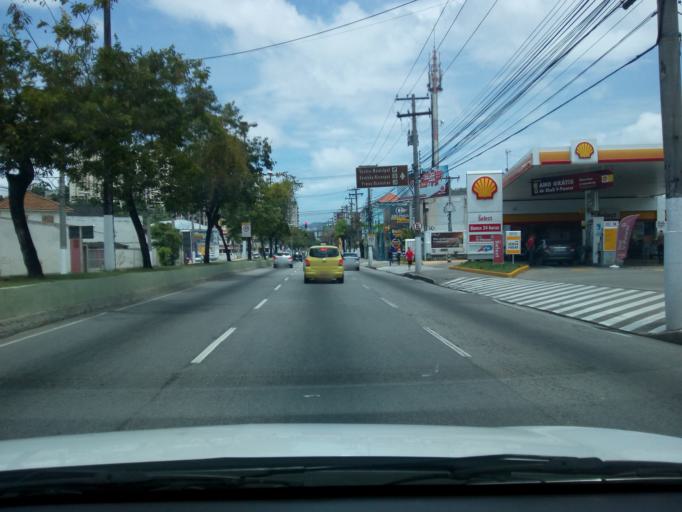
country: BR
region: Rio de Janeiro
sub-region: Niteroi
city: Niteroi
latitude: -22.8878
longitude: -43.1149
